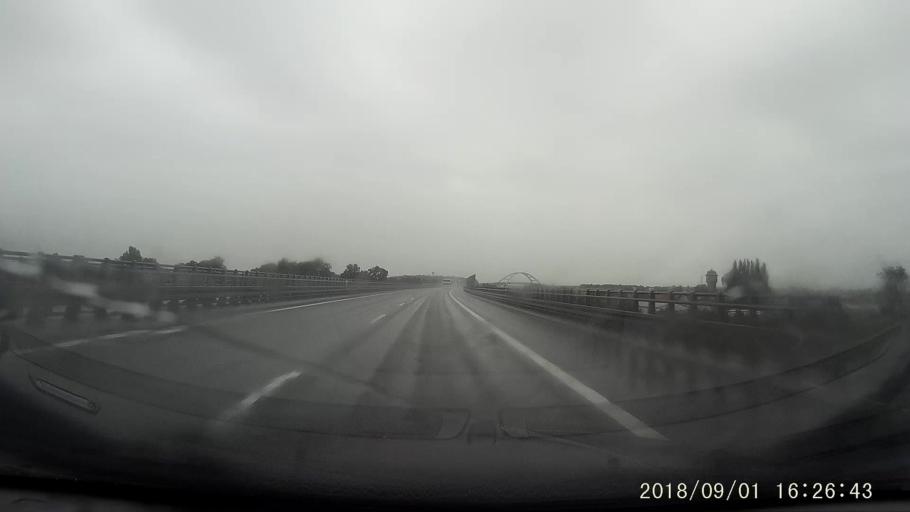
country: PL
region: Lubusz
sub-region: Powiat swiebodzinski
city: Swiebodzin
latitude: 52.2521
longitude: 15.5545
